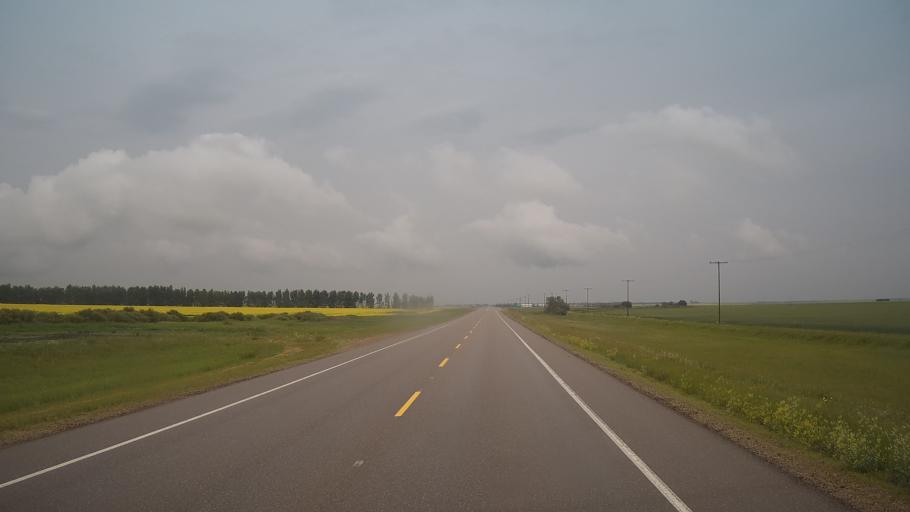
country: CA
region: Saskatchewan
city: Wilkie
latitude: 52.3424
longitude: -108.7138
